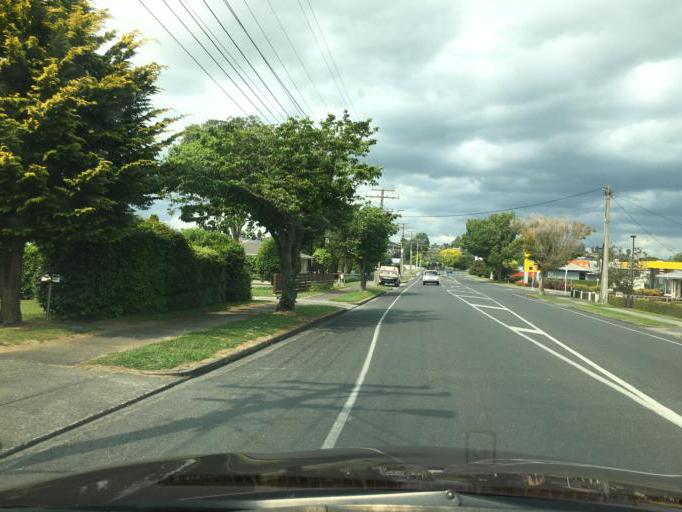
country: NZ
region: Waikato
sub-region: Waipa District
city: Cambridge
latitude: -38.0068
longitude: 175.3377
